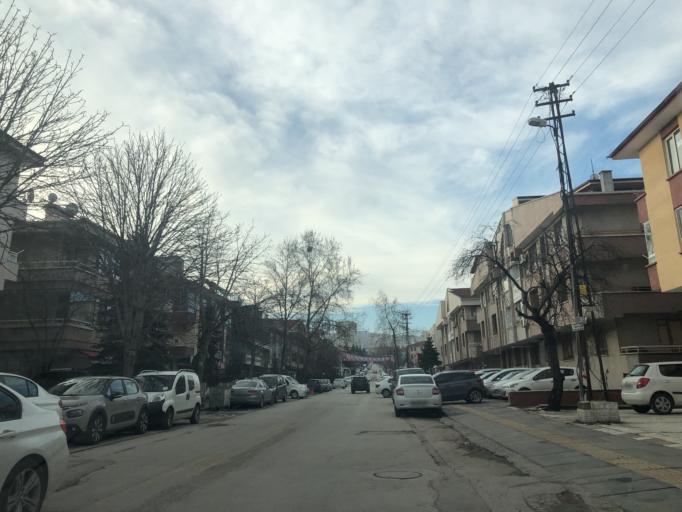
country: TR
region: Ankara
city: Ankara
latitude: 39.8936
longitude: 32.8270
